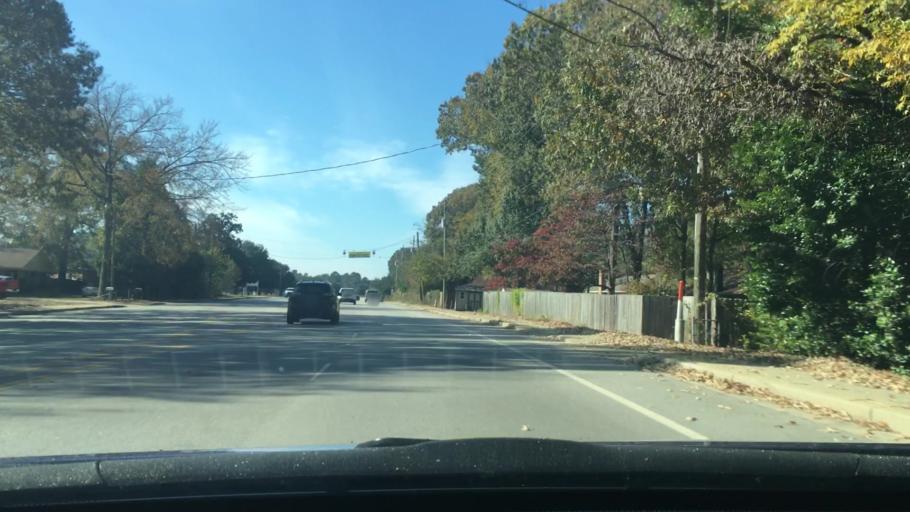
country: US
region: South Carolina
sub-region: Sumter County
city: South Sumter
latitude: 33.9030
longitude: -80.3889
